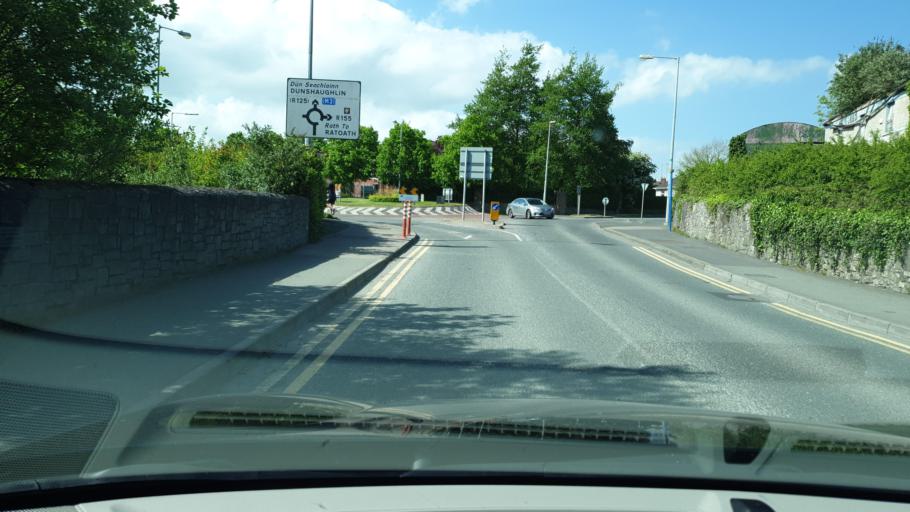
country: IE
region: Leinster
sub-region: An Mhi
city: Ratoath
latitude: 53.5051
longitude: -6.4670
